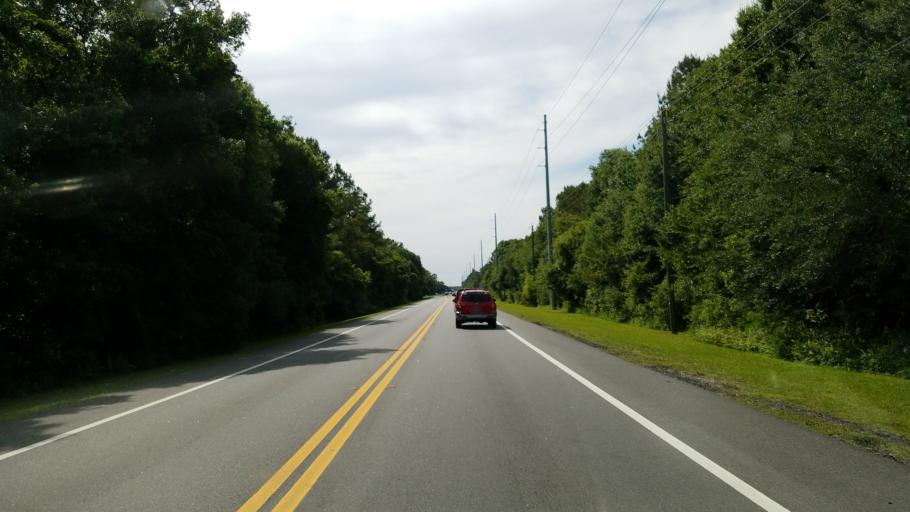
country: US
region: Florida
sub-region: Hillsborough County
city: Fish Hawk
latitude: 27.8554
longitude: -82.1895
